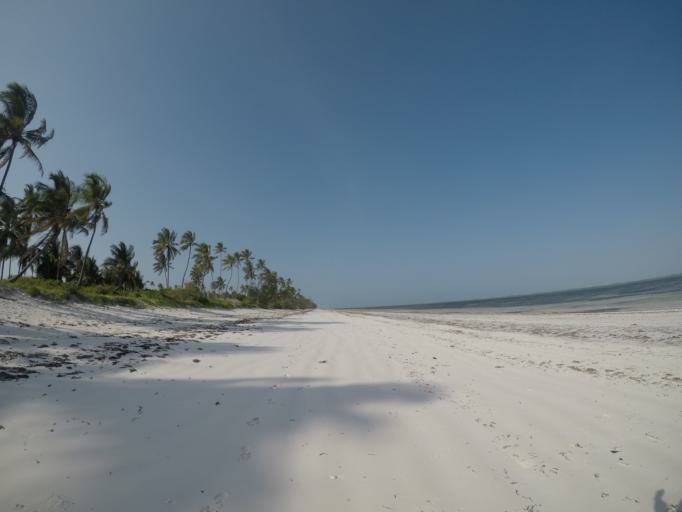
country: TZ
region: Zanzibar Central/South
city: Nganane
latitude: -6.2133
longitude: 39.5340
